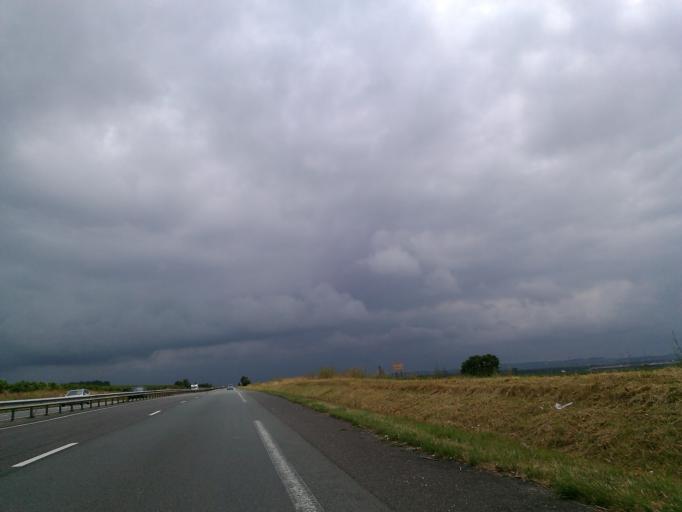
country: FR
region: Poitou-Charentes
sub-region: Departement de la Charente
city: Gensac-la-Pallue
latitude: 45.6699
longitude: -0.2536
